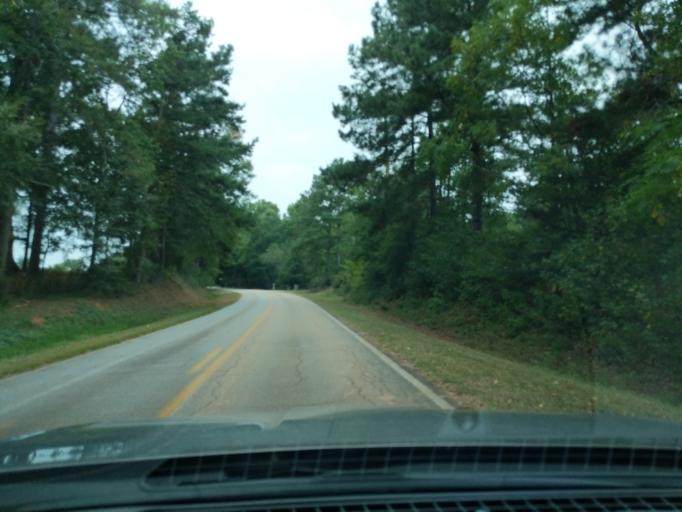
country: US
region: Georgia
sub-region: Columbia County
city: Appling
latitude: 33.6360
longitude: -82.3962
